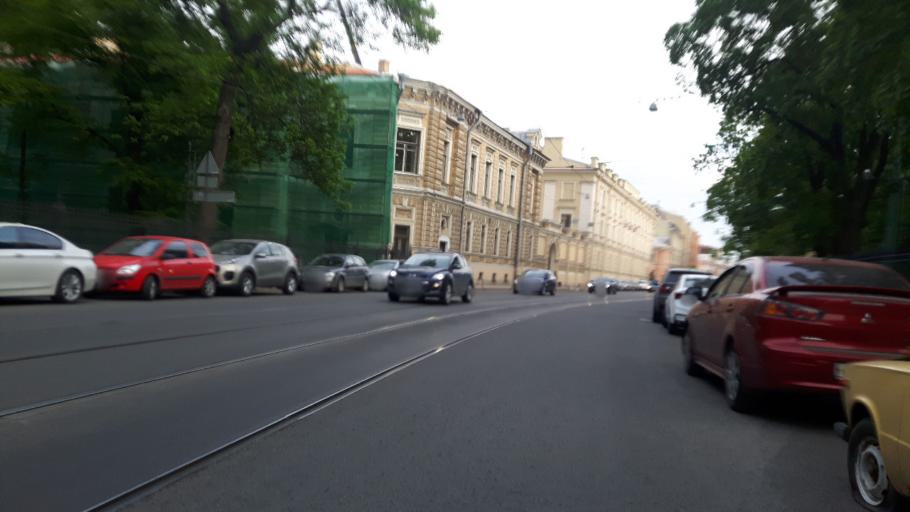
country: RU
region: St.-Petersburg
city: Saint Petersburg
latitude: 59.9391
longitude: 30.3366
